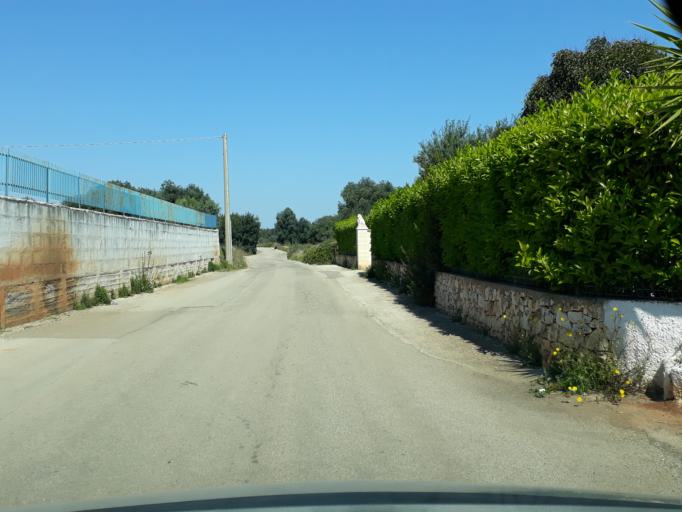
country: IT
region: Apulia
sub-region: Provincia di Brindisi
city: Fasano
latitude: 40.8274
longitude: 17.3824
